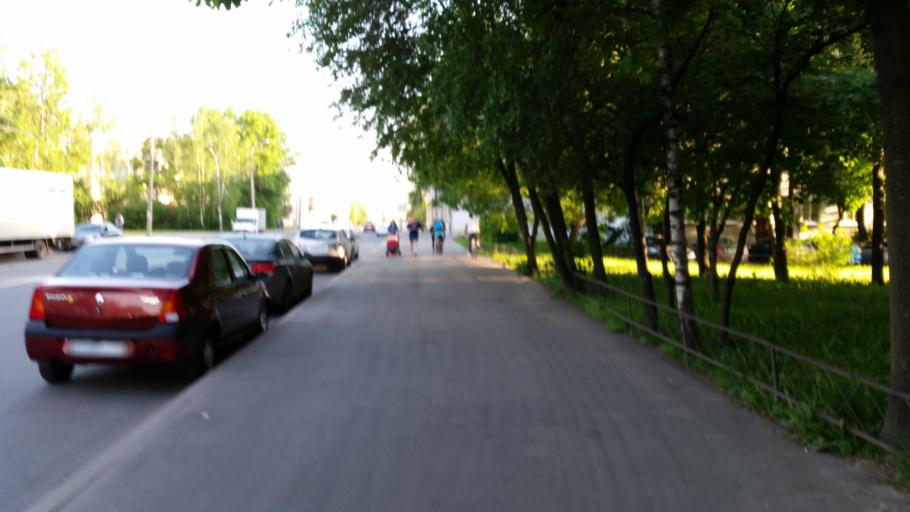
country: RU
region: St.-Petersburg
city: Sosnovaya Polyana
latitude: 59.8443
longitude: 30.1468
